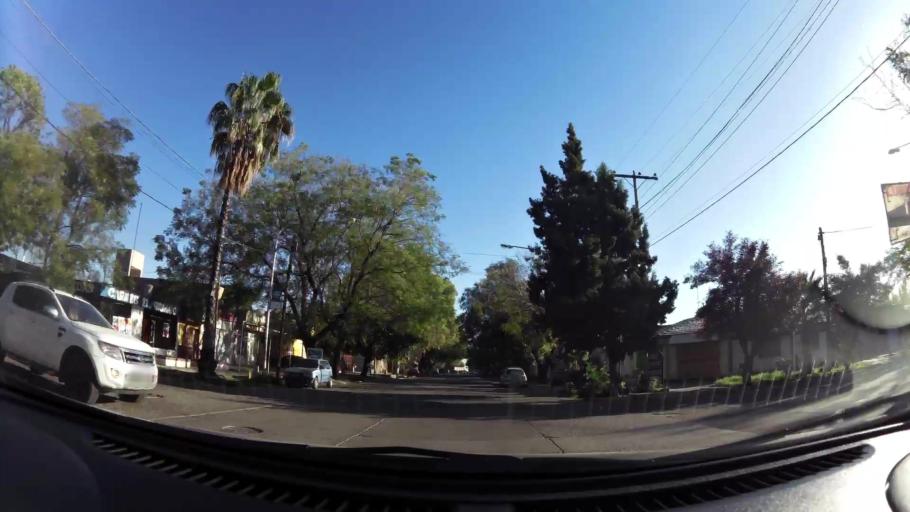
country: AR
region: Mendoza
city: Las Heras
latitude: -32.8654
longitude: -68.8223
